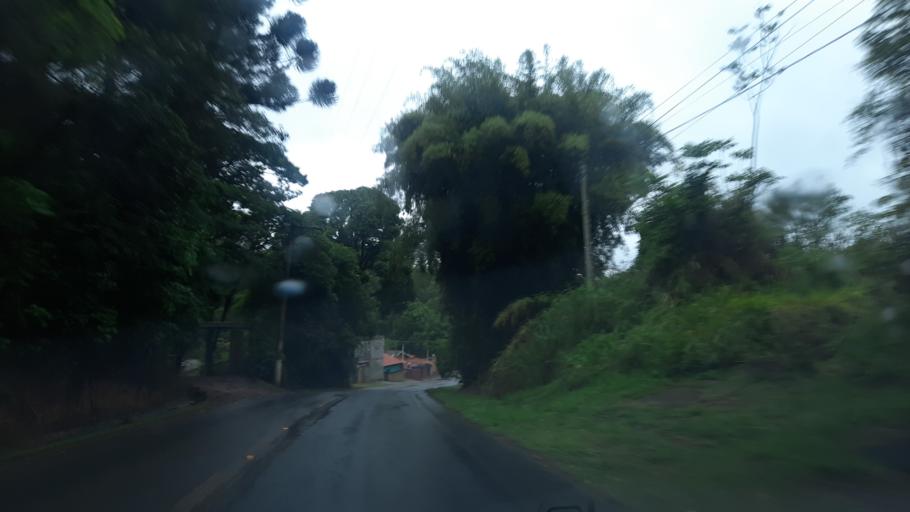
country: BR
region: Sao Paulo
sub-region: Atibaia
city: Atibaia
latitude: -23.0856
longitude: -46.5297
